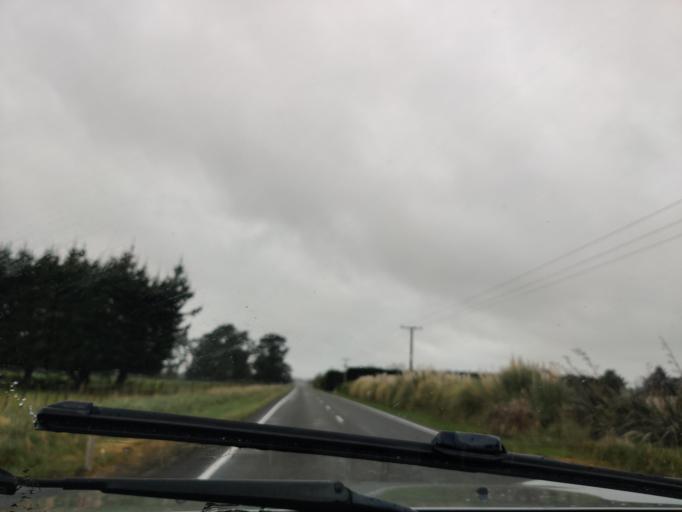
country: NZ
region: Hawke's Bay
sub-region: Hastings District
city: Hastings
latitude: -40.0193
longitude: 176.3434
